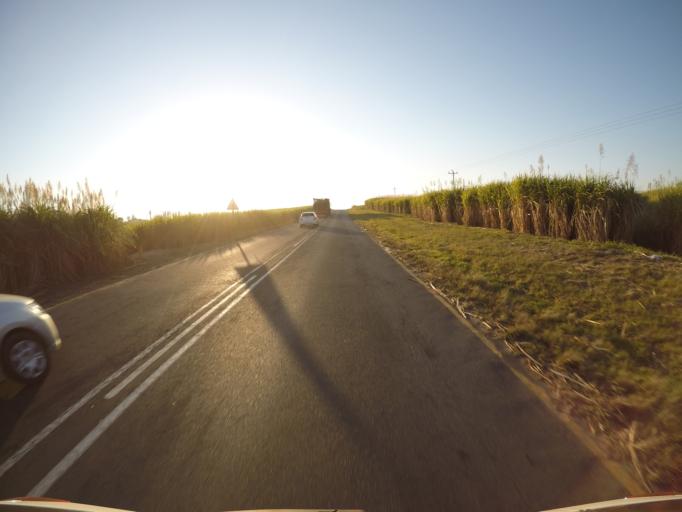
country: ZA
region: KwaZulu-Natal
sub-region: uThungulu District Municipality
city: eSikhawini
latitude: -28.9490
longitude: 31.7156
